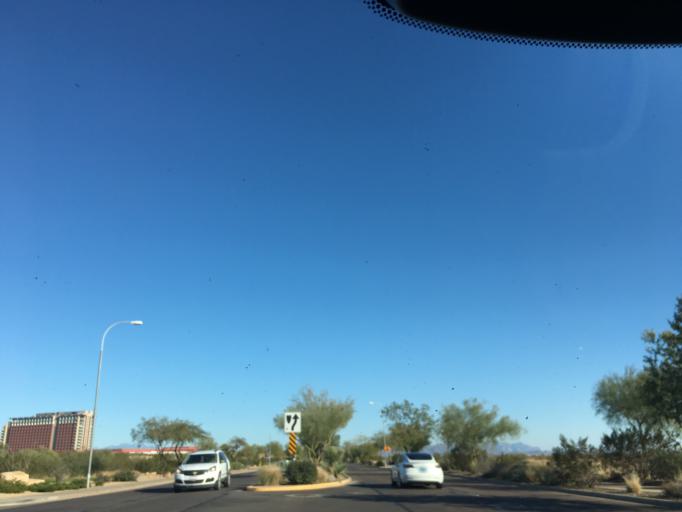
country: US
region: Arizona
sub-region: Maricopa County
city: Scottsdale
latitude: 33.5385
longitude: -111.8774
